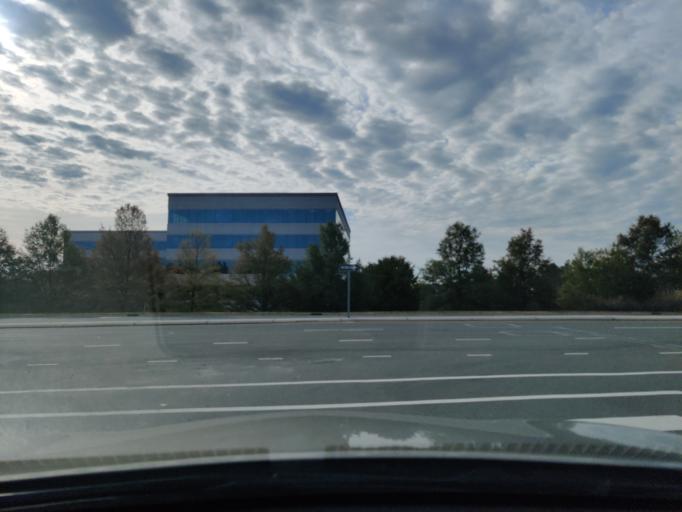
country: US
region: North Carolina
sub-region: Wake County
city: Morrisville
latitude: 35.8772
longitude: -78.8643
